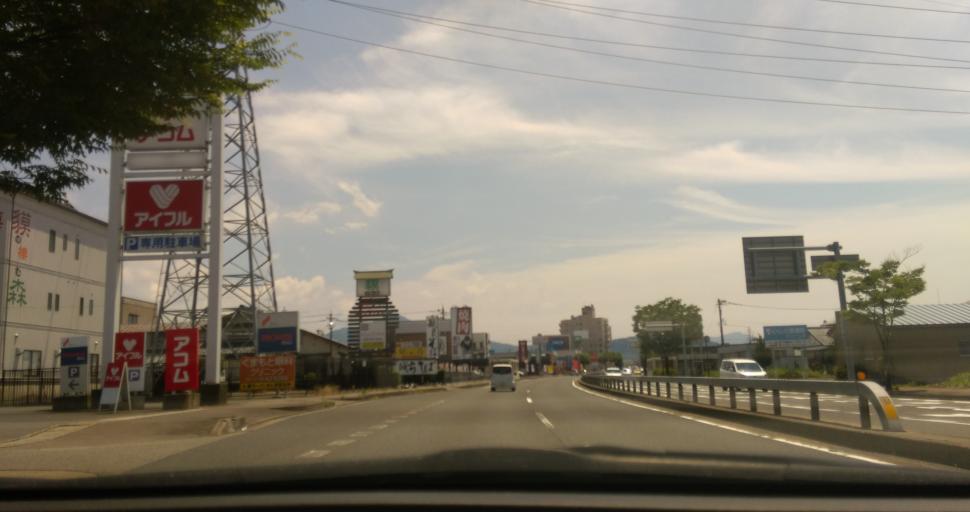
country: JP
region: Fukui
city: Sabae
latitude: 35.9463
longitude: 136.1946
